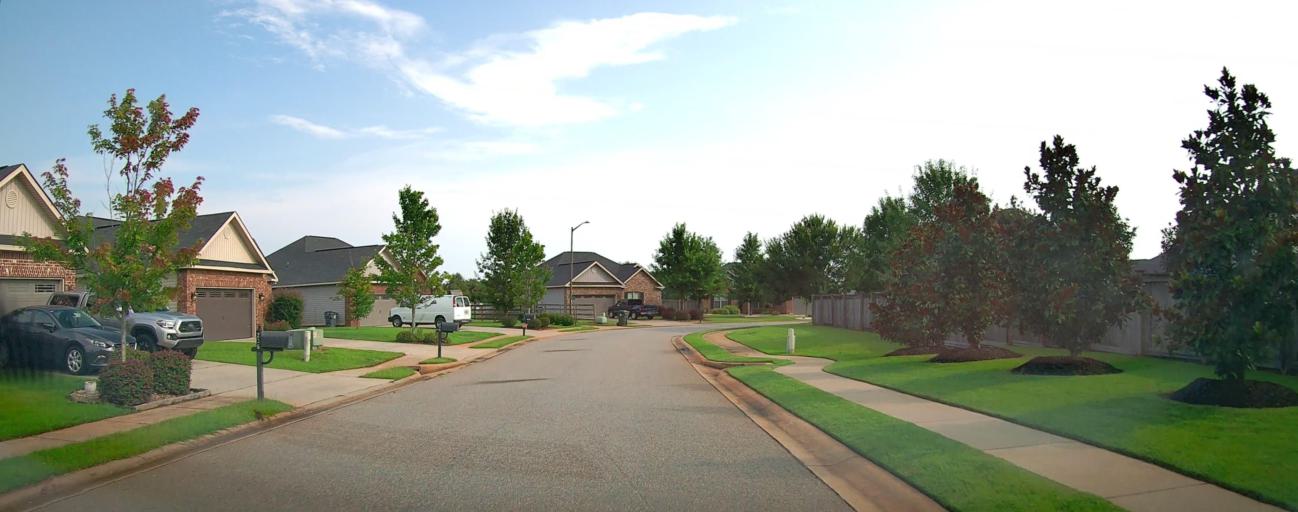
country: US
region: Georgia
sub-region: Houston County
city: Centerville
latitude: 32.6277
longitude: -83.7192
